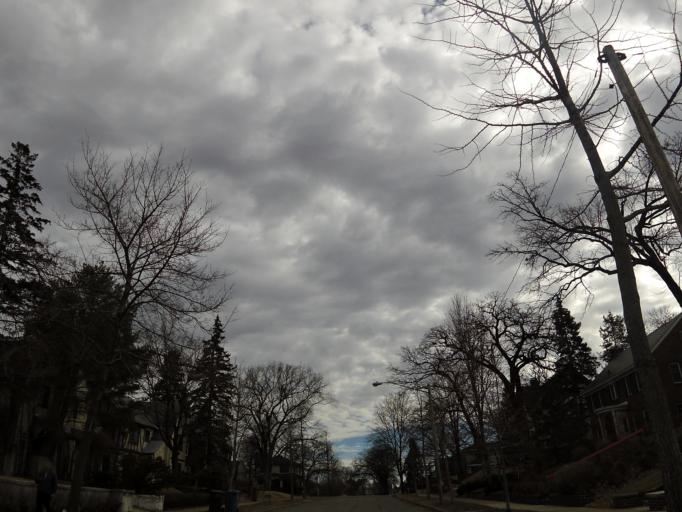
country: US
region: Minnesota
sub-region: Hennepin County
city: Richfield
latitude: 44.9150
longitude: -93.3087
